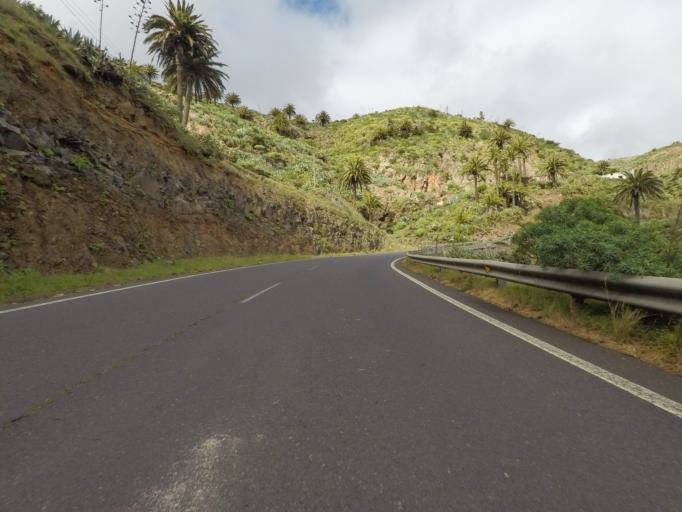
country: ES
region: Canary Islands
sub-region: Provincia de Santa Cruz de Tenerife
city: Alajero
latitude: 28.0954
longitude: -17.1907
